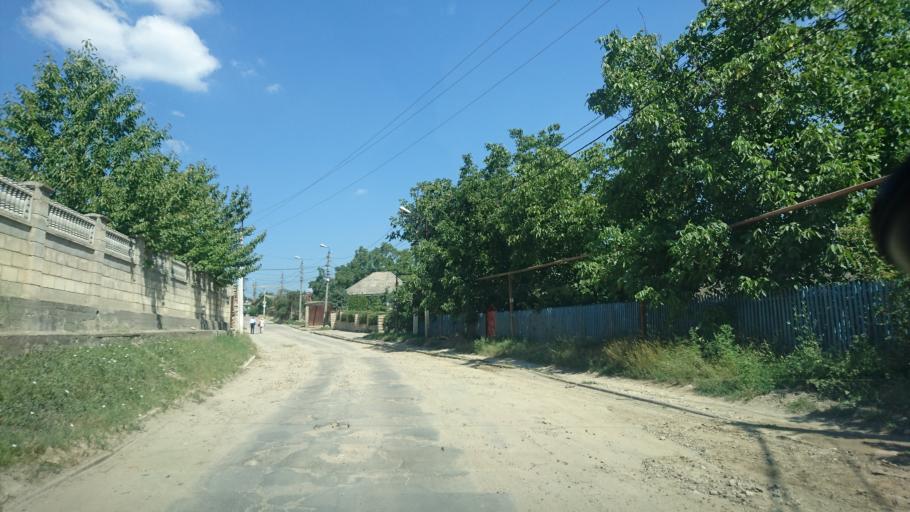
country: MD
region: Chisinau
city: Vatra
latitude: 47.0173
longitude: 28.7670
